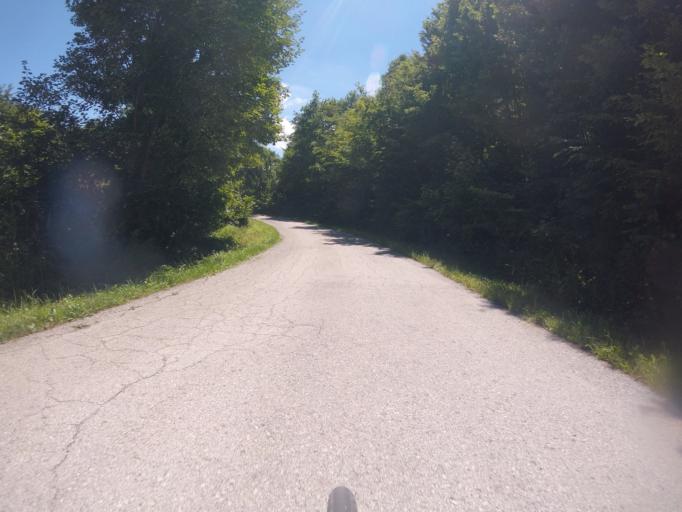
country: SI
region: Metlika
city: Metlika
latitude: 45.7162
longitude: 15.3838
